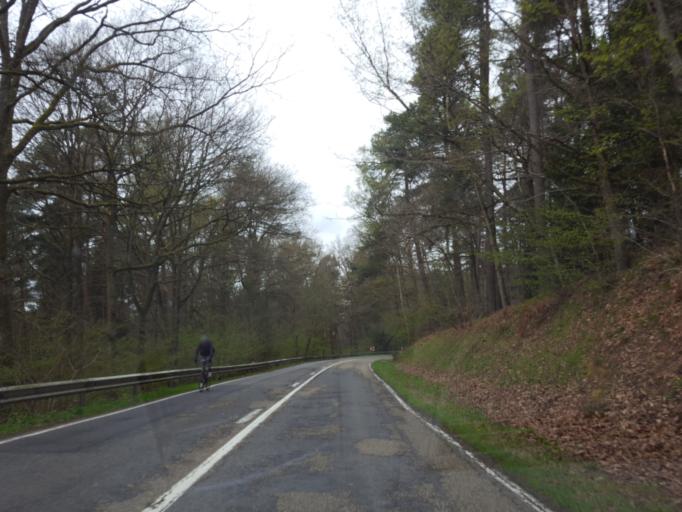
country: BE
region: Wallonia
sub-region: Province de Liege
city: Stoumont
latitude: 50.4138
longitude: 5.7940
